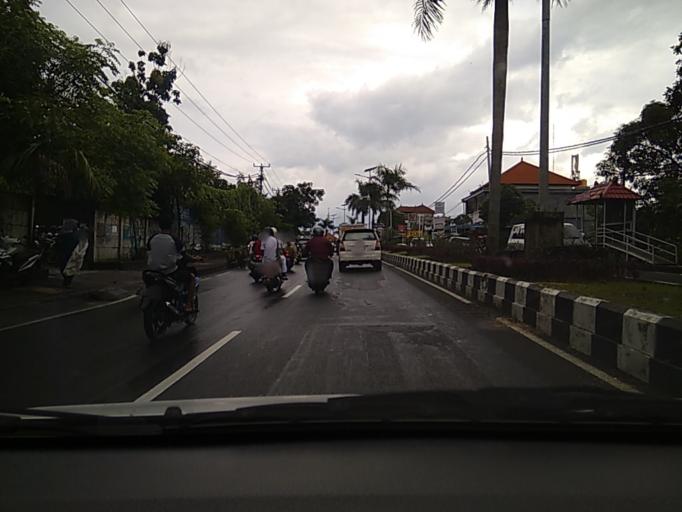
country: ID
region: Bali
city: Bualu
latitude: -8.7860
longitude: 115.2031
